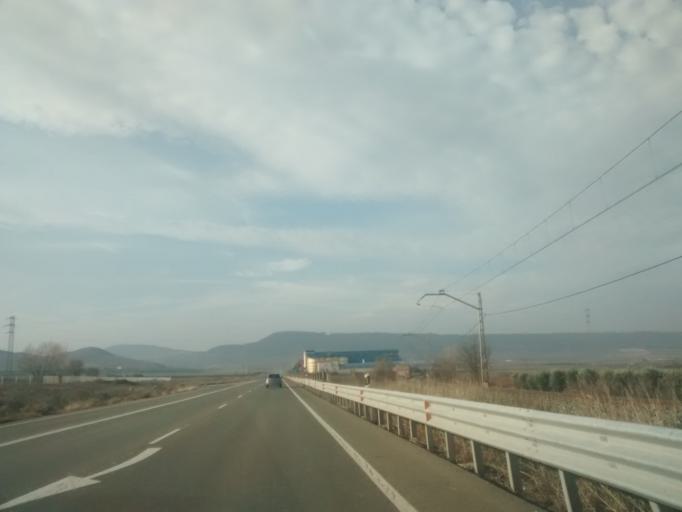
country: ES
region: La Rioja
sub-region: Provincia de La Rioja
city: Fuenmayor
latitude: 42.4627
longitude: -2.5929
